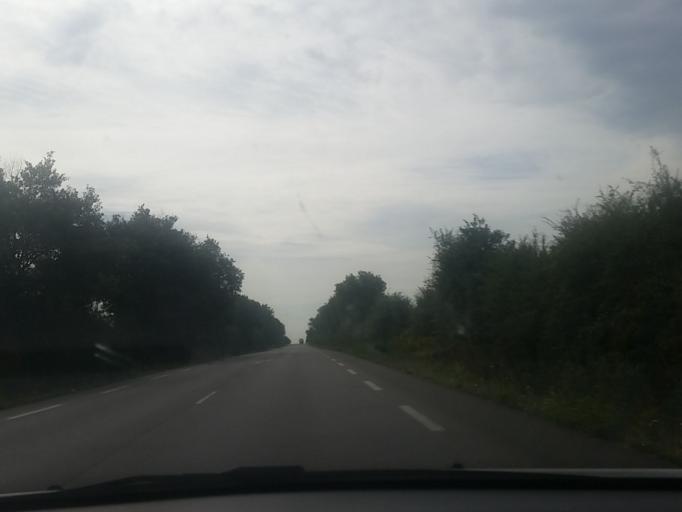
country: FR
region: Pays de la Loire
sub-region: Departement de la Vendee
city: Sainte-Cecile
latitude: 46.7661
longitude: -1.1068
